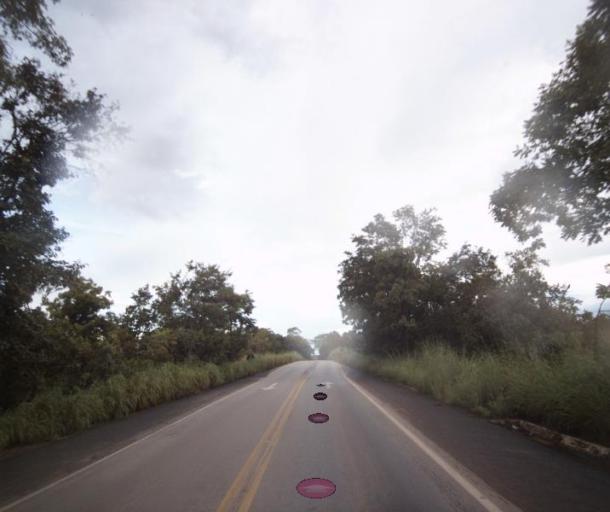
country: BR
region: Goias
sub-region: Porangatu
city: Porangatu
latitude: -13.9225
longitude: -49.0694
